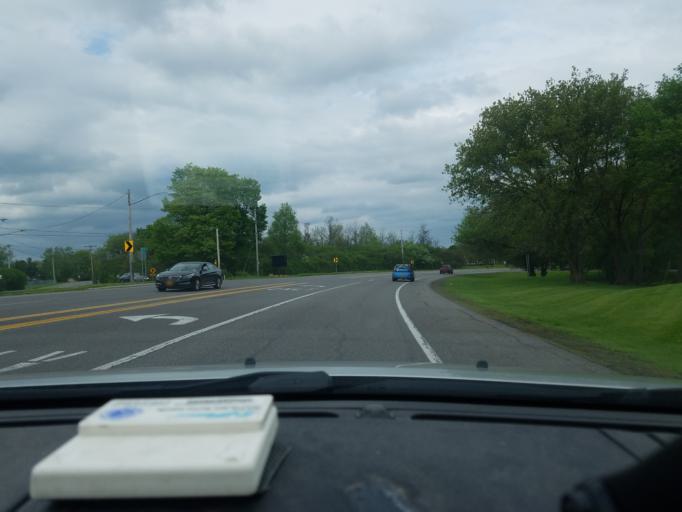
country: US
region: New York
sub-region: Onondaga County
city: Galeville
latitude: 43.1202
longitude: -76.1829
